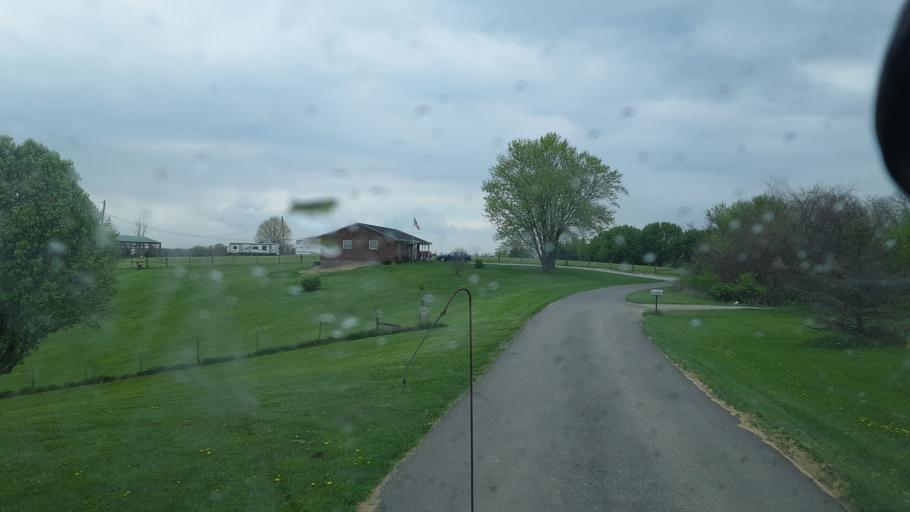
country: US
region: Kentucky
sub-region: Owen County
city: Owenton
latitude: 38.6740
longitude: -84.7840
